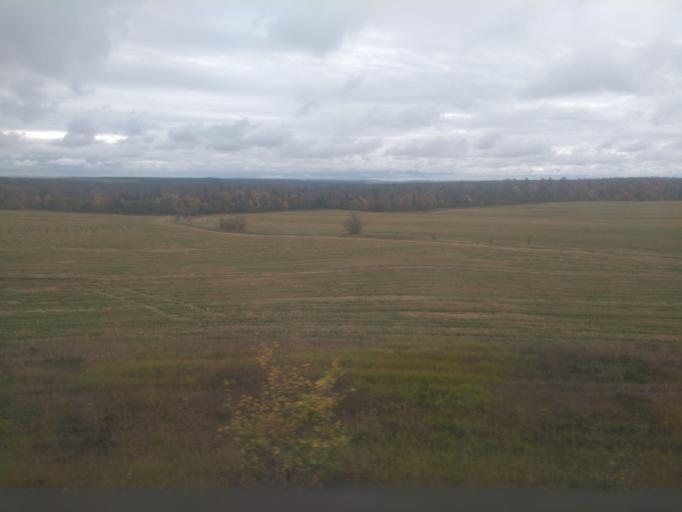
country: RU
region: Udmurtiya
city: Alnashi
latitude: 56.1527
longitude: 52.5786
